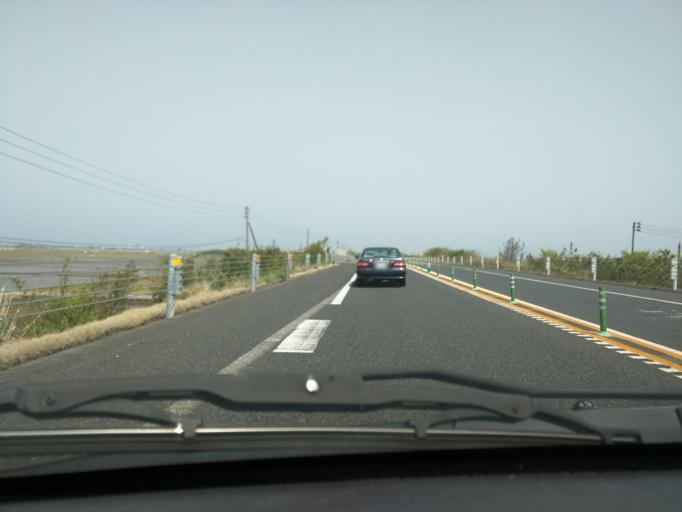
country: JP
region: Niigata
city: Kameda-honcho
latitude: 37.8413
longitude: 139.0666
